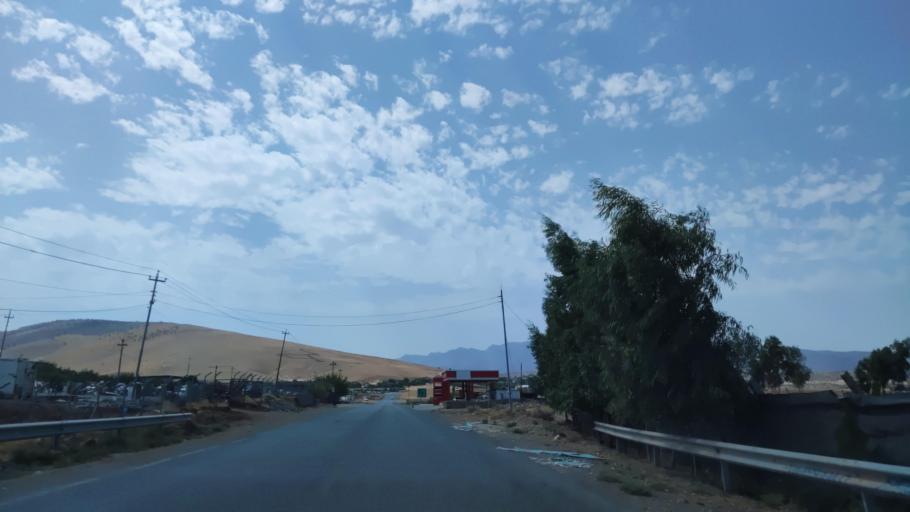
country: IQ
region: Arbil
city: Shaqlawah
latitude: 36.4745
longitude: 44.3975
